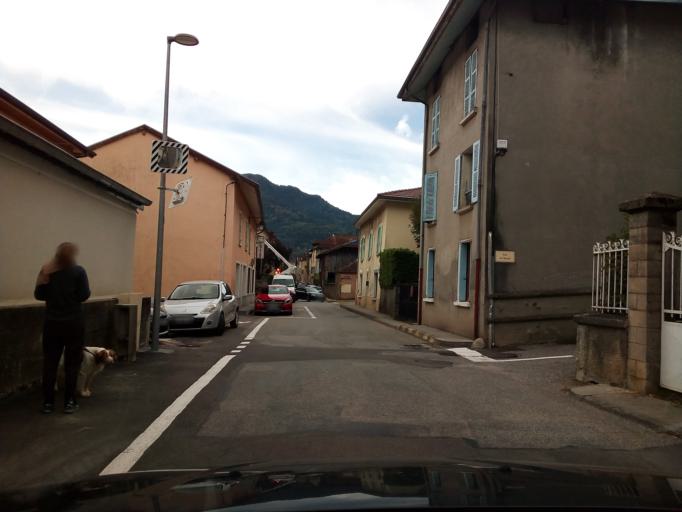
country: FR
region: Rhone-Alpes
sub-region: Departement de l'Isere
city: Allevard
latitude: 45.3753
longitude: 6.0483
